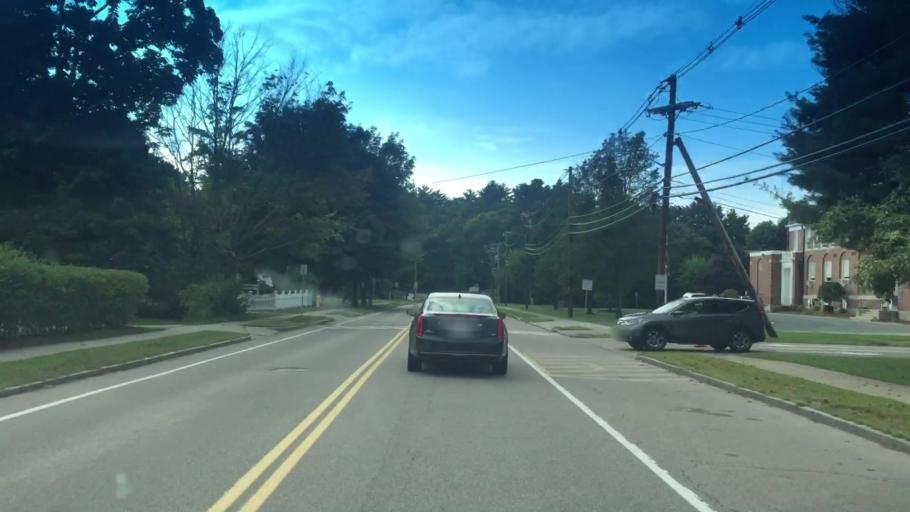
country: US
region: Massachusetts
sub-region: Norfolk County
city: Westwood
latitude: 42.2067
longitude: -71.2353
